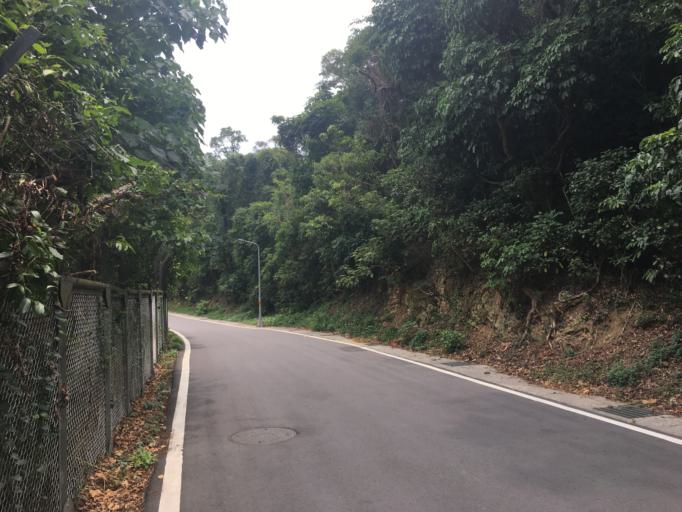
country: TW
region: Taipei
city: Taipei
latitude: 25.0891
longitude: 121.5528
